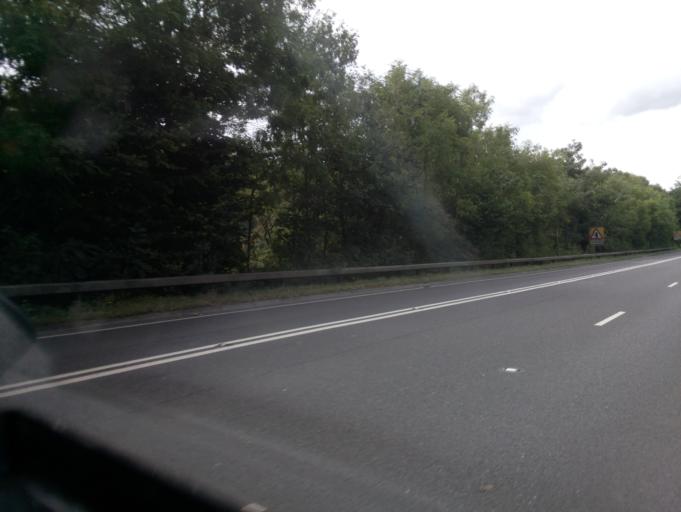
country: GB
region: England
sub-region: Somerset
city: Yeovil
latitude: 50.9616
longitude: -2.6522
